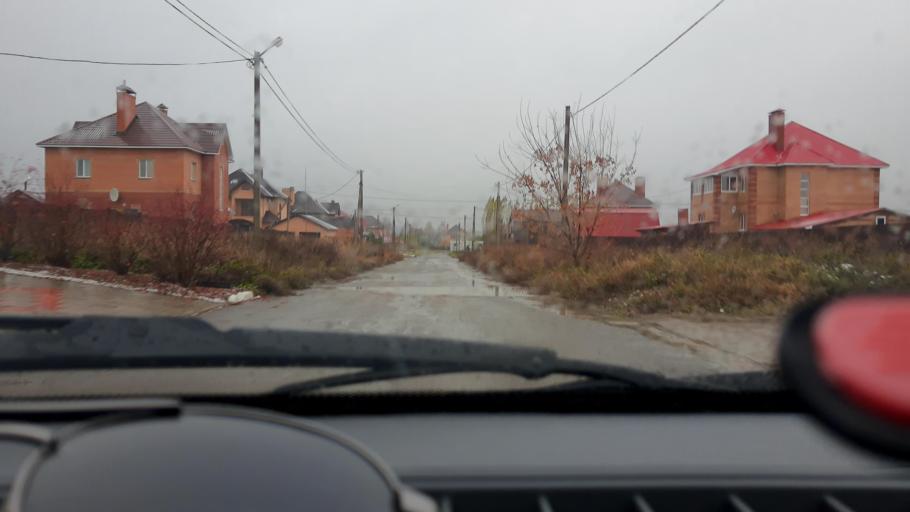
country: RU
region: Bashkortostan
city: Kabakovo
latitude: 54.6225
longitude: 56.1284
